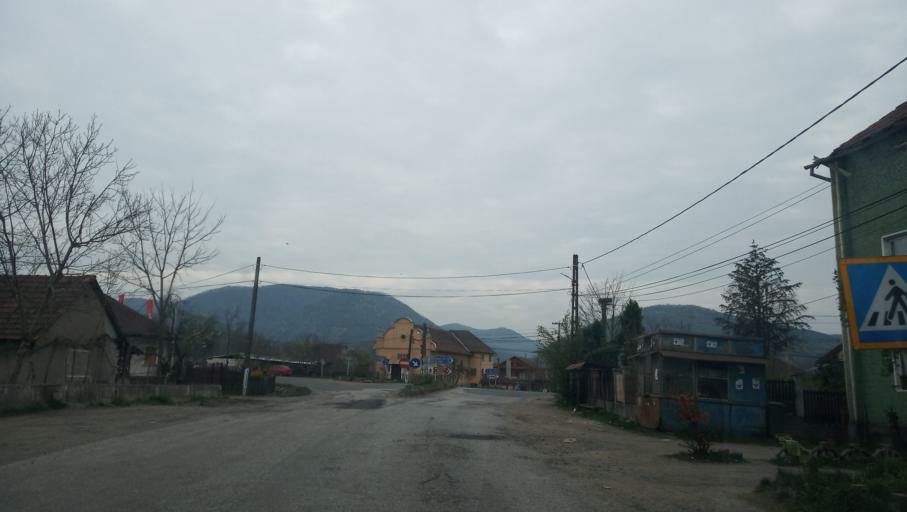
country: RO
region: Arad
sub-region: Comuna Varfurile
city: Varfurile
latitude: 46.3059
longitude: 22.5262
